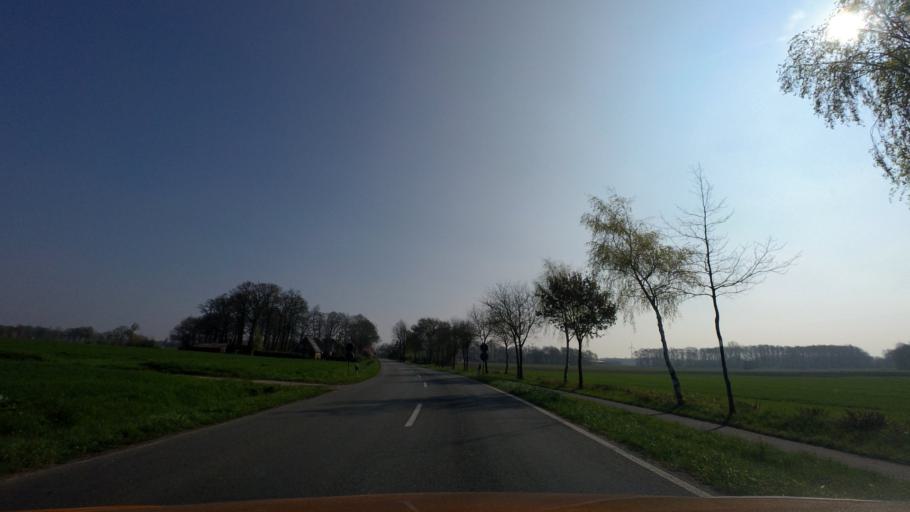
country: DE
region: Lower Saxony
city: Bakum
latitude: 52.7461
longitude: 8.2018
